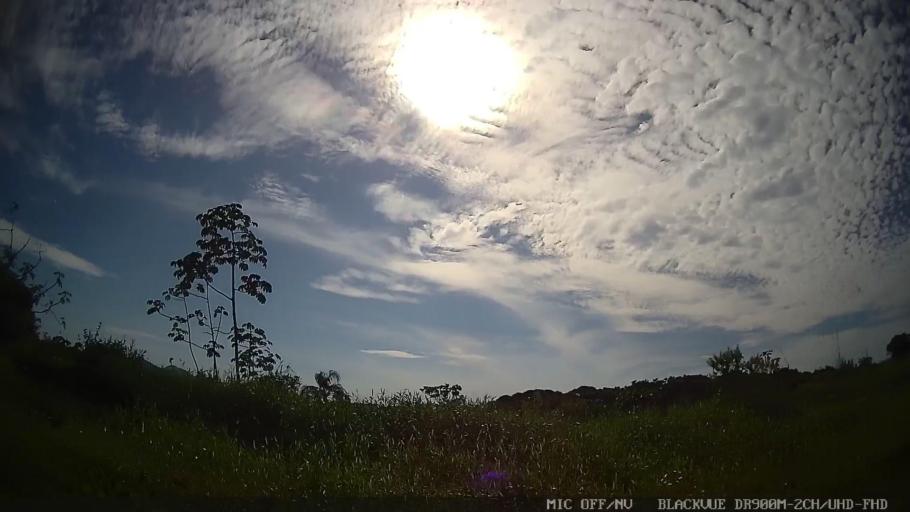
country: BR
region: Sao Paulo
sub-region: Iguape
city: Iguape
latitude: -24.7679
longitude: -47.5916
